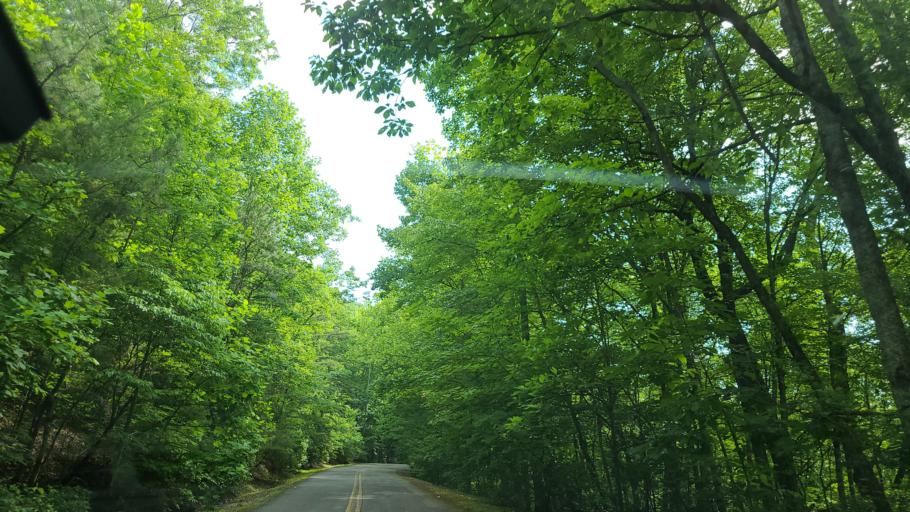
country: US
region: Kentucky
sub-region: Bell County
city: Pineville
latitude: 36.7506
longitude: -83.7156
